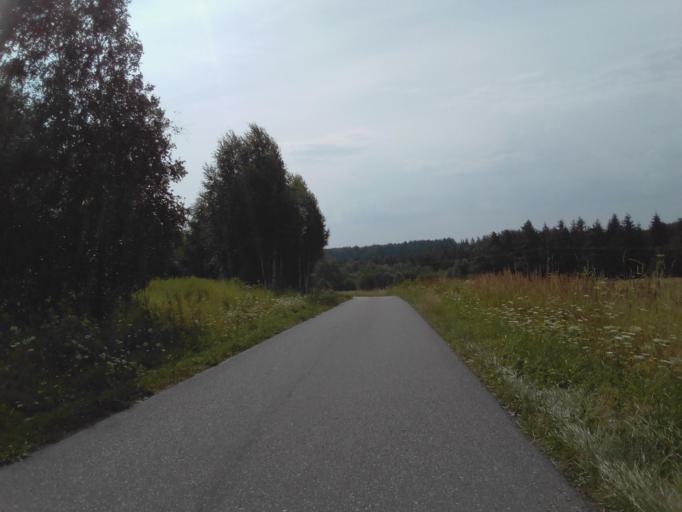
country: PL
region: Subcarpathian Voivodeship
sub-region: Powiat strzyzowski
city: Frysztak
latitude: 49.8630
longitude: 21.5354
